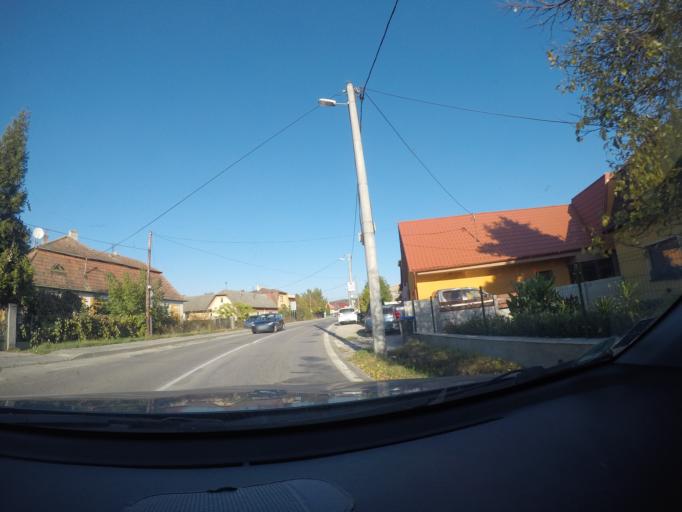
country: SK
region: Trenciansky
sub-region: Okres Trencin
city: Trencin
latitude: 48.9041
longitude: 18.0384
